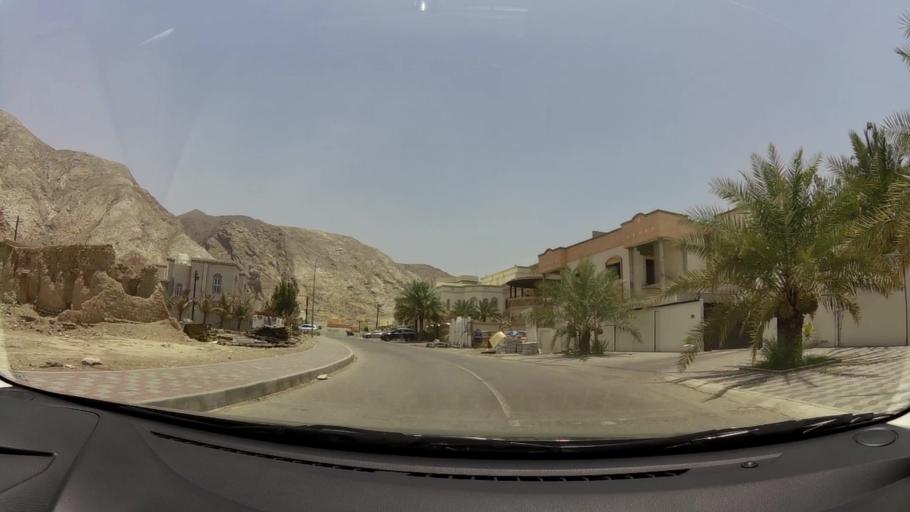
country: OM
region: Muhafazat Masqat
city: Bawshar
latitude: 23.5525
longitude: 58.4107
